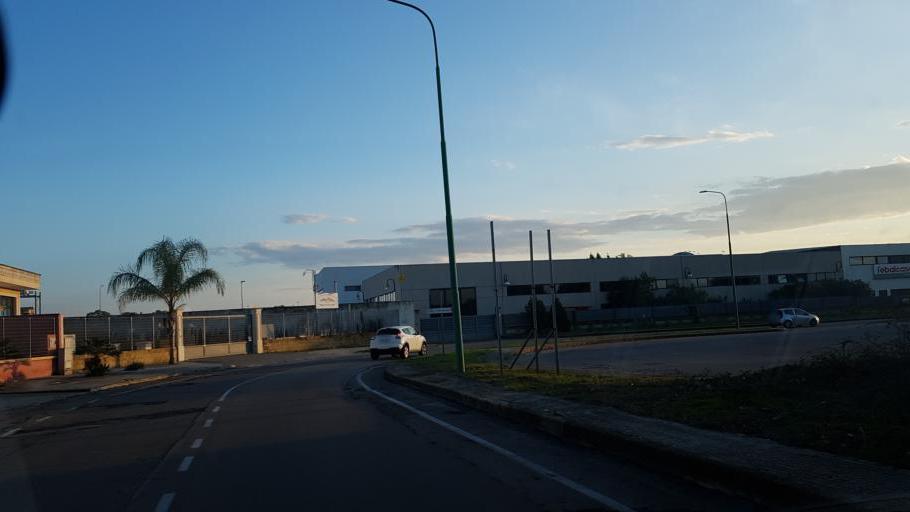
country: IT
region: Apulia
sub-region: Provincia di Lecce
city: Giorgilorio
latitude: 40.3820
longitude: 18.1400
